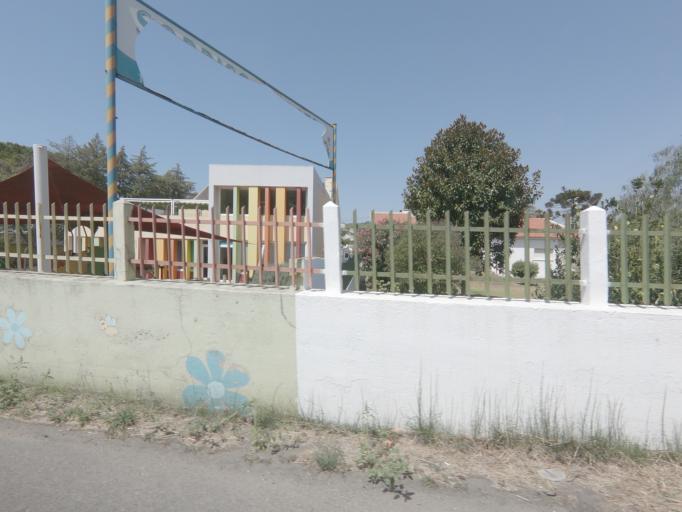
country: PT
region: Setubal
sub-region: Setubal
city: Setubal
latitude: 38.5328
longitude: -8.9039
